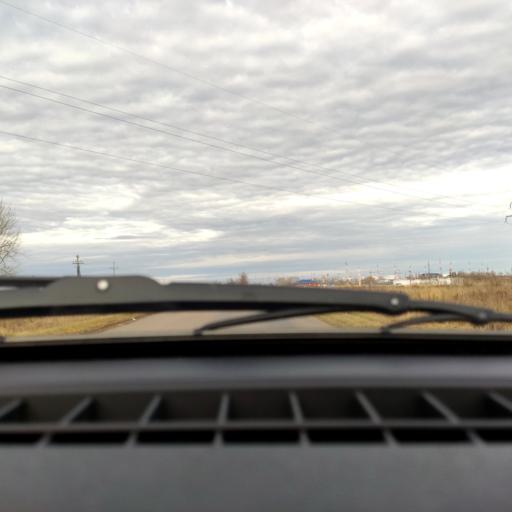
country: RU
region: Bashkortostan
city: Blagoveshchensk
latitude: 54.8941
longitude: 56.1506
